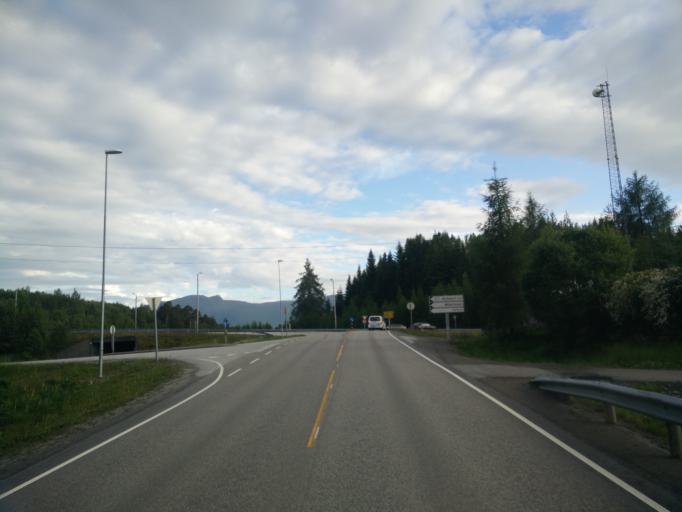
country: NO
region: More og Romsdal
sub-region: Kristiansund
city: Rensvik
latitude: 63.0127
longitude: 8.0016
